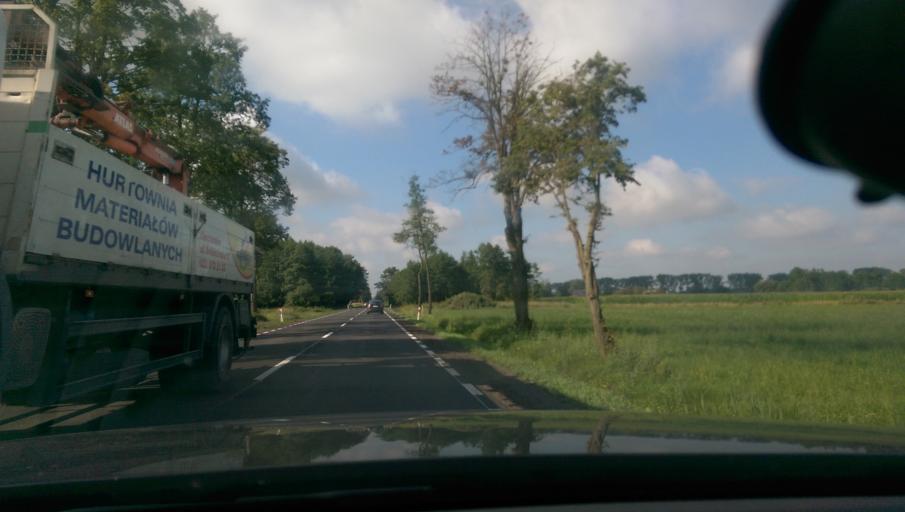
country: PL
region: Masovian Voivodeship
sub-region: Powiat ciechanowski
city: Ojrzen
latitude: 52.7329
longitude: 20.5162
